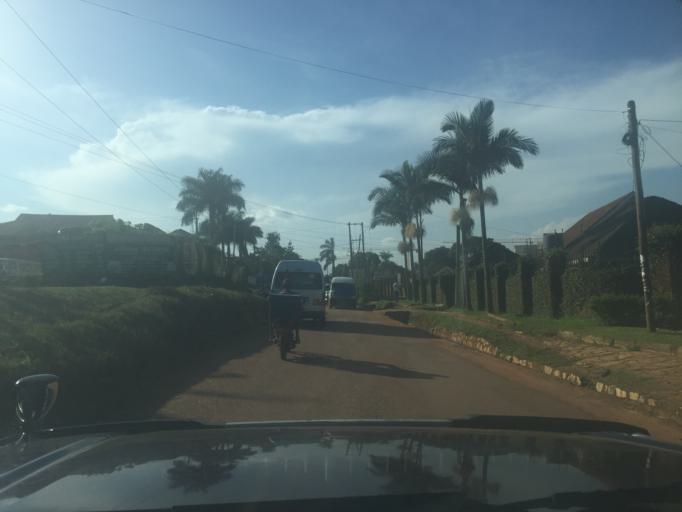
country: UG
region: Central Region
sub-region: Kampala District
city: Kampala
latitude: 0.2975
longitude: 32.5943
